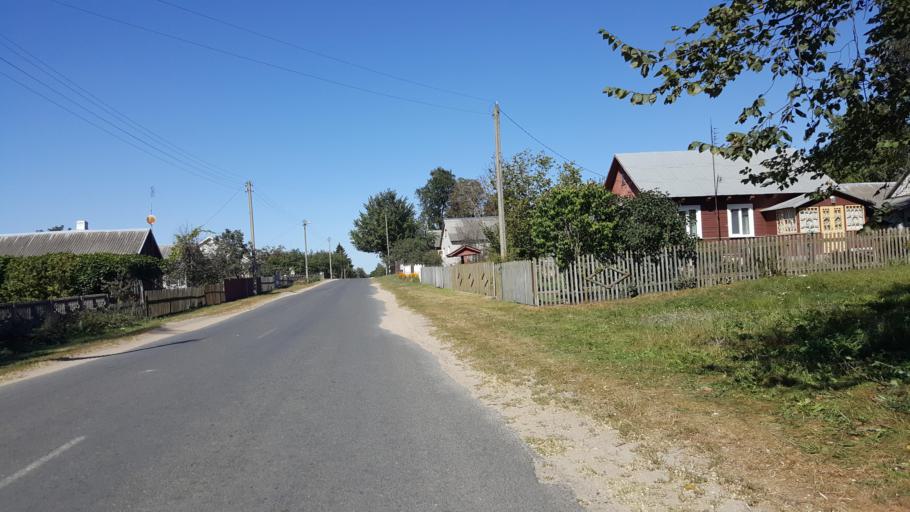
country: PL
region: Lublin Voivodeship
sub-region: Powiat bialski
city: Rokitno
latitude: 52.2356
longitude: 23.3413
